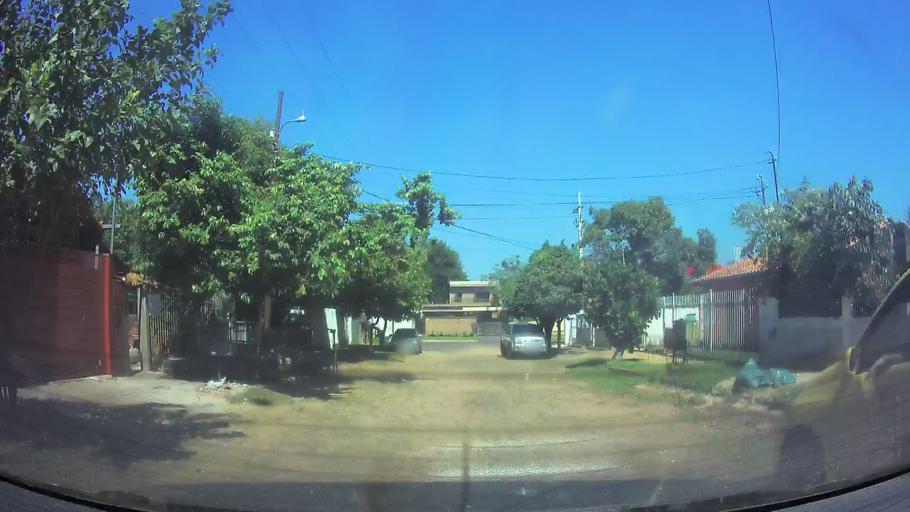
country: PY
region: Central
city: Fernando de la Mora
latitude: -25.3045
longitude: -57.5304
